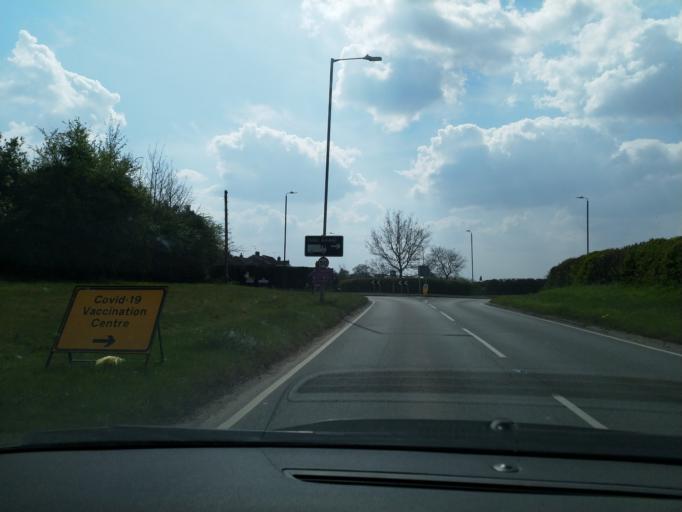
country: GB
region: England
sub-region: Warwickshire
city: Royal Leamington Spa
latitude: 52.3170
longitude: -1.5177
